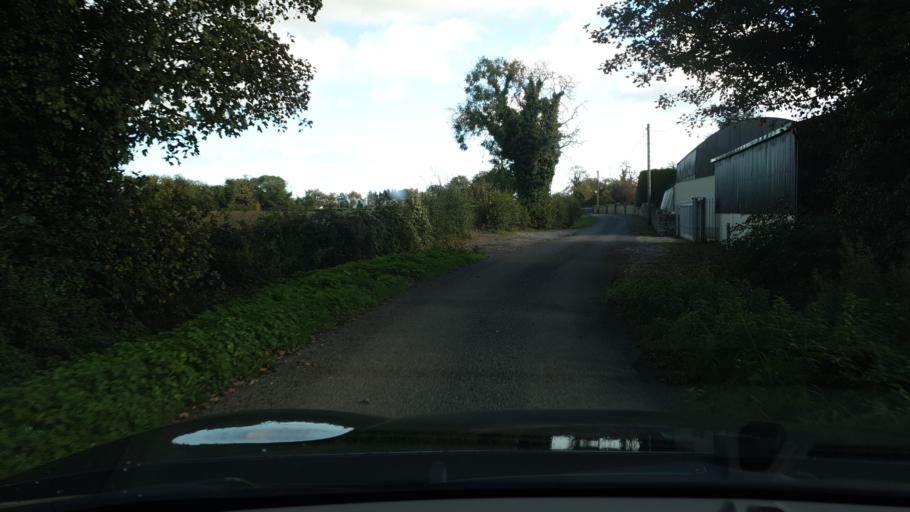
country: IE
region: Leinster
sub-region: Fingal County
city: Swords
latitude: 53.4914
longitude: -6.2609
